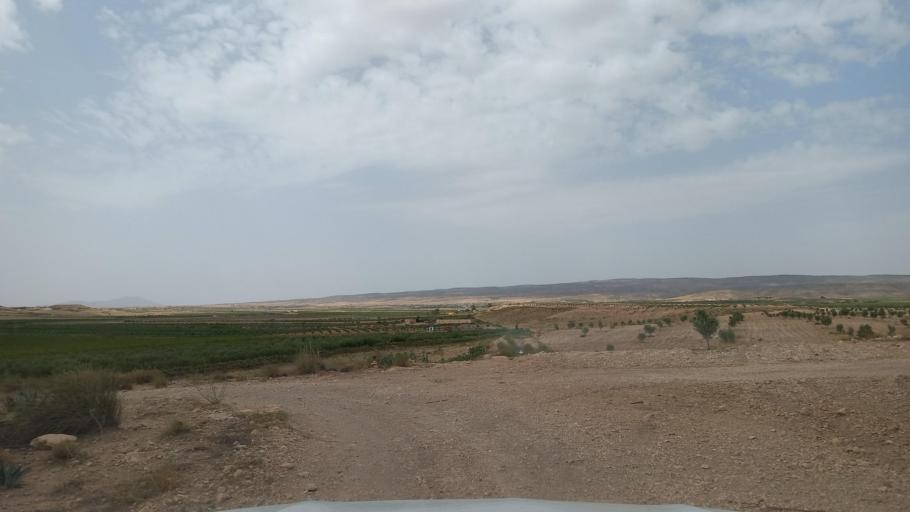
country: TN
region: Al Qasrayn
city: Kasserine
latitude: 35.2920
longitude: 9.0017
